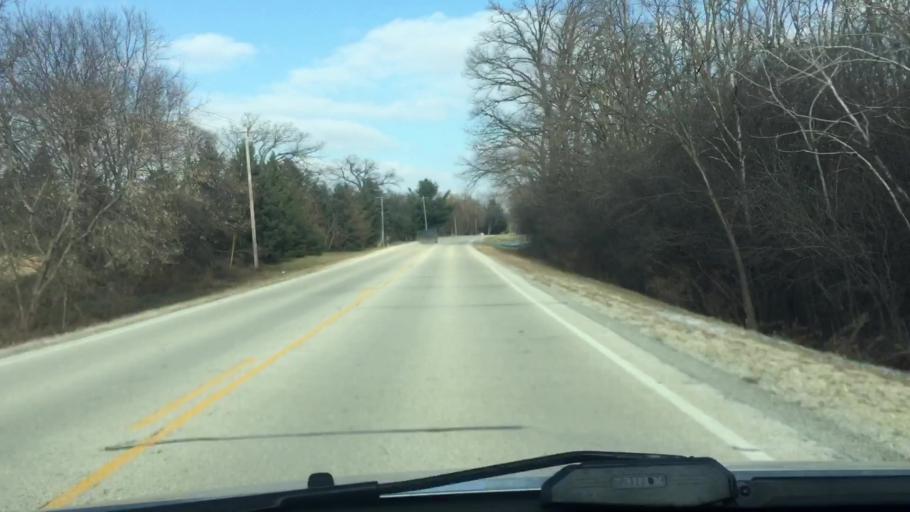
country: US
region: Wisconsin
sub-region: Jefferson County
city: Palmyra
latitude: 42.8944
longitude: -88.5534
